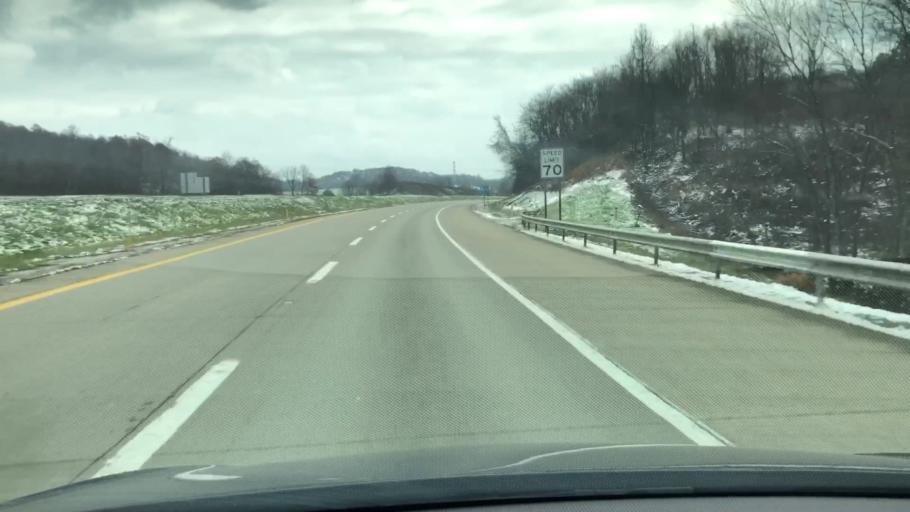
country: US
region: Pennsylvania
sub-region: Westmoreland County
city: Delmont
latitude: 40.3726
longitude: -79.5593
